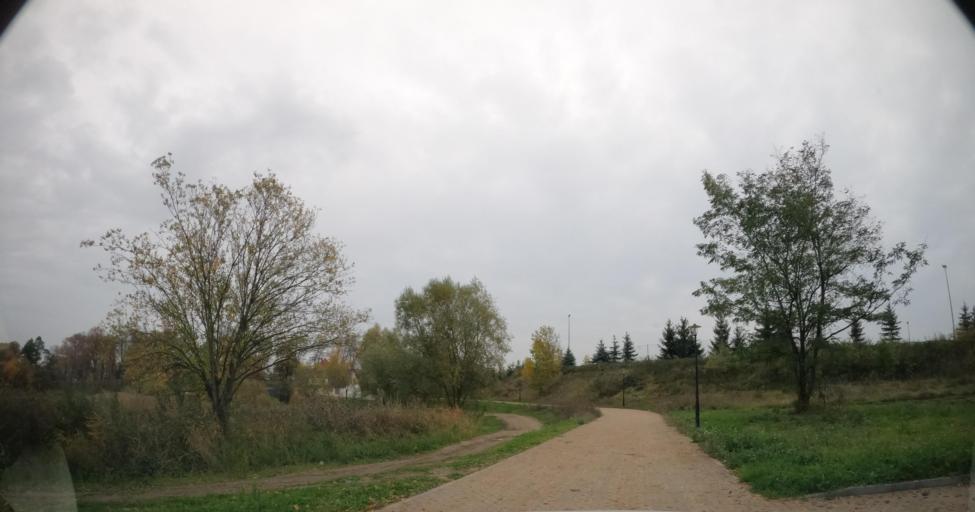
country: PL
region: West Pomeranian Voivodeship
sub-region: Powiat choszczenski
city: Pelczyce
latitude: 53.0375
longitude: 15.2973
